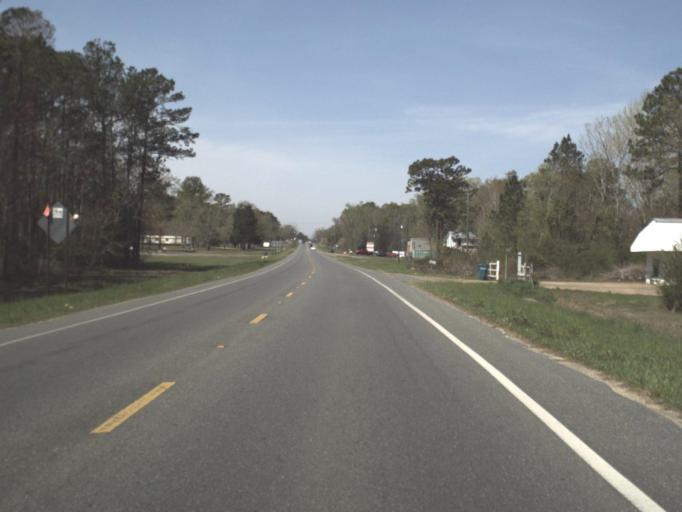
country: US
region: Florida
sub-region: Holmes County
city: Bonifay
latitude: 30.7878
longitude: -85.6664
